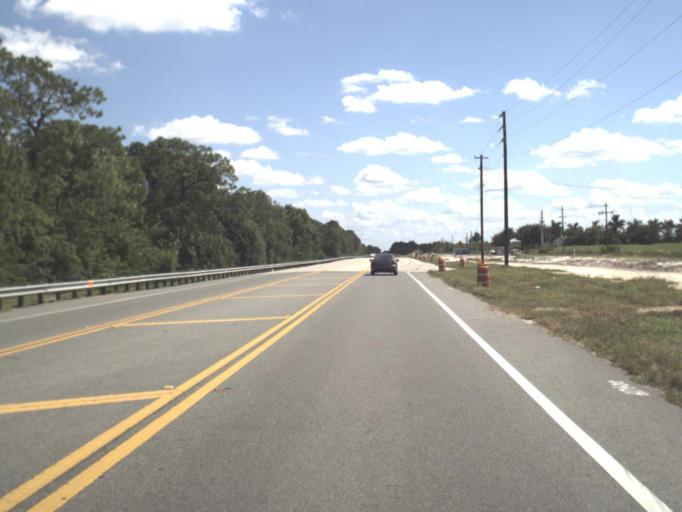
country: US
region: Florida
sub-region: Collier County
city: Lely Resort
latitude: 26.0367
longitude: -81.6576
